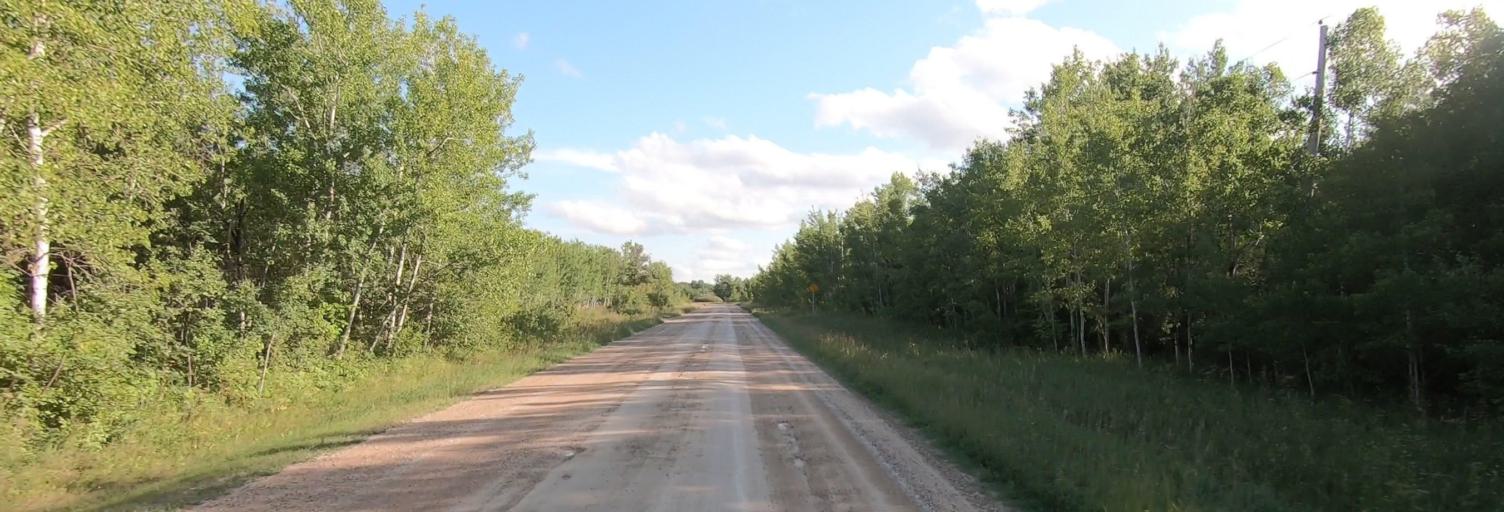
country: CA
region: Manitoba
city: Selkirk
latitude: 50.2390
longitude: -96.8440
